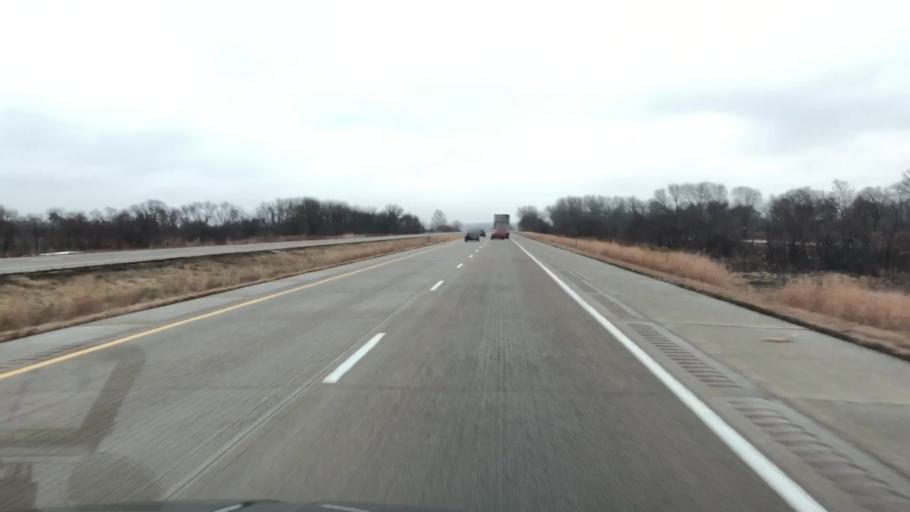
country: US
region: Nebraska
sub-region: Burt County
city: Tekamah
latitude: 41.8446
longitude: -96.0932
